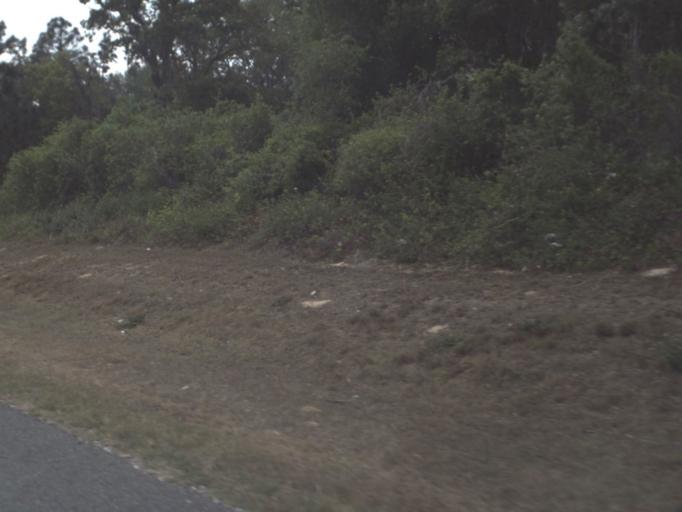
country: US
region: Florida
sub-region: Lake County
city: Groveland
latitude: 28.6028
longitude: -81.8388
